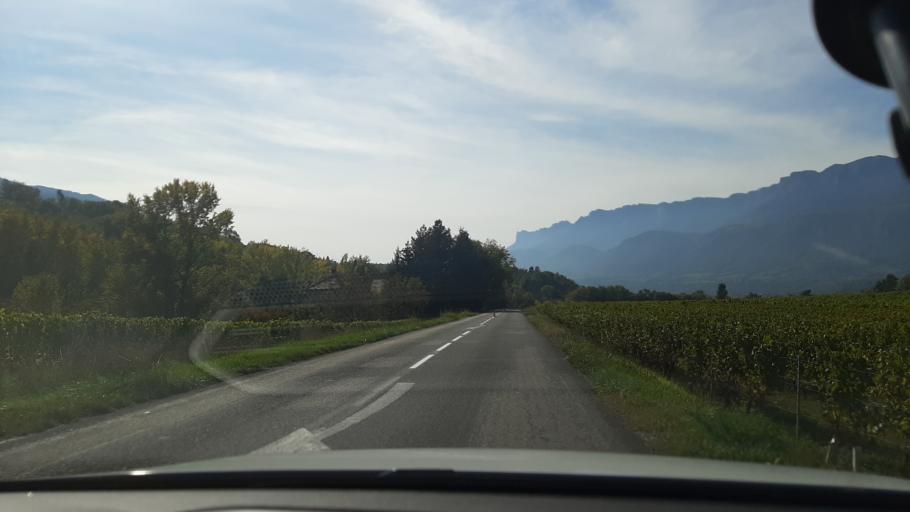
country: FR
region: Rhone-Alpes
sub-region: Departement de l'Isere
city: Pontcharra
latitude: 45.4523
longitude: 6.0518
